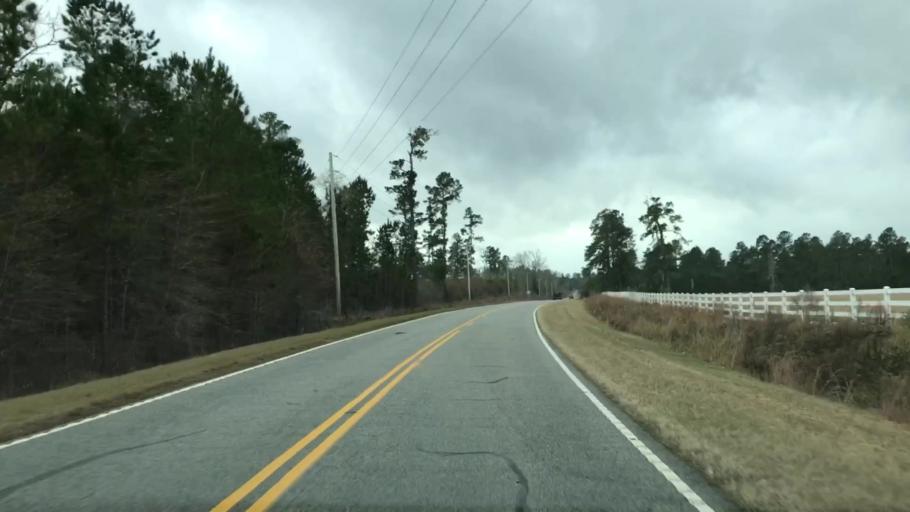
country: US
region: South Carolina
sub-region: Florence County
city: Johnsonville
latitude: 33.6488
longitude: -79.4198
